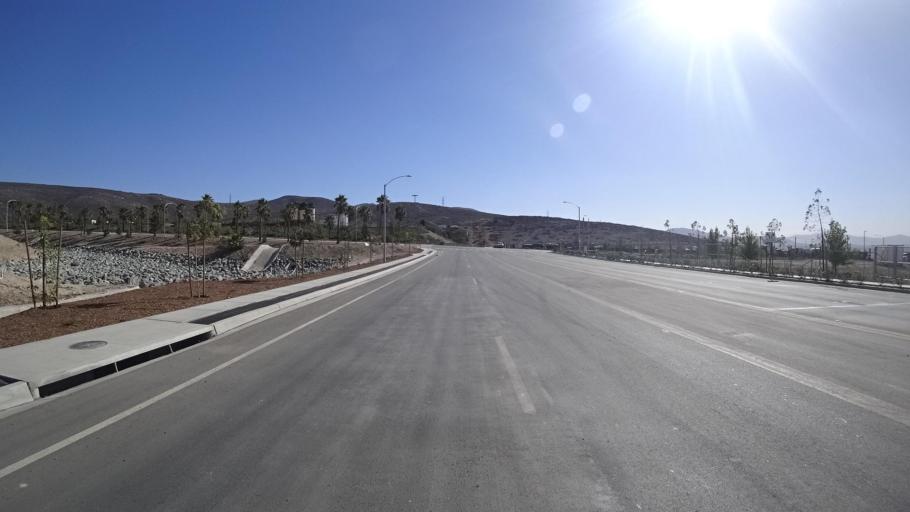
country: MX
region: Baja California
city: Tijuana
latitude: 32.5674
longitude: -116.9138
